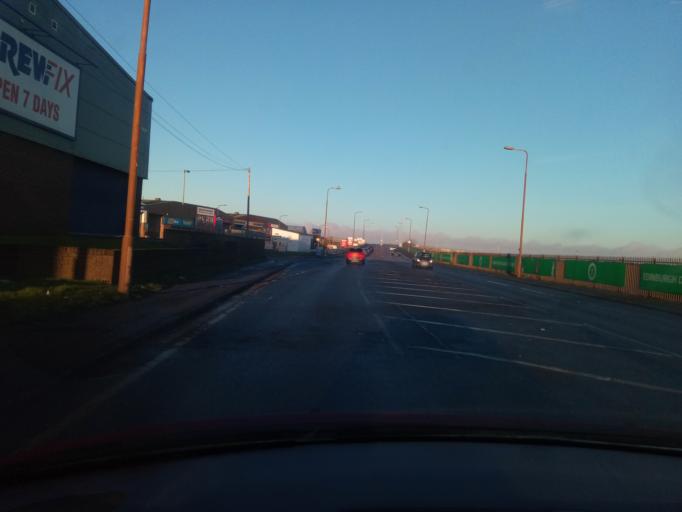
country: GB
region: Scotland
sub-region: West Lothian
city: Seafield
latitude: 55.9642
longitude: -3.1304
